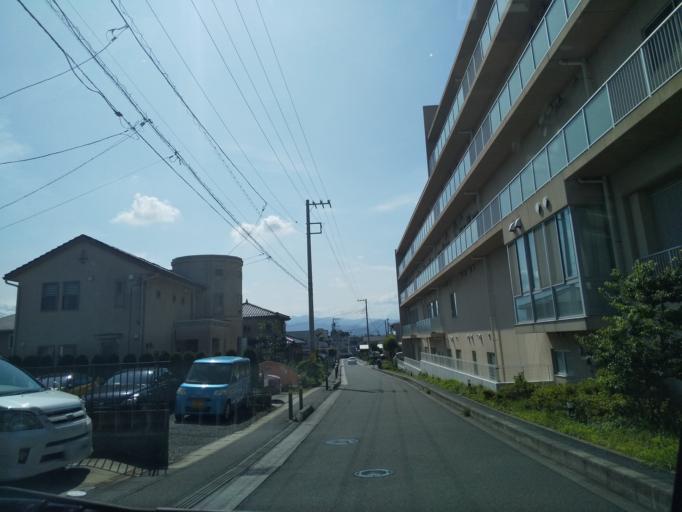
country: JP
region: Kanagawa
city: Zama
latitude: 35.4642
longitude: 139.4160
